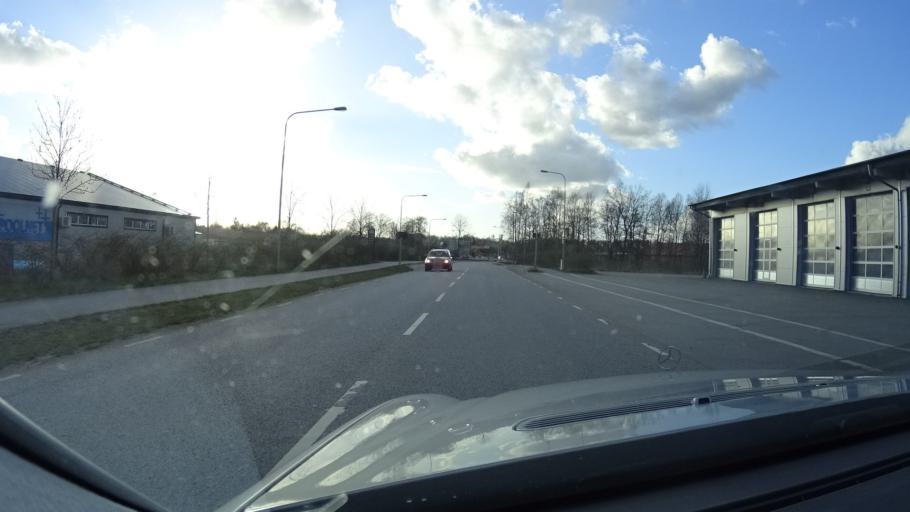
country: SE
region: Skane
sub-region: Hoors Kommun
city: Satofta
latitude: 55.9250
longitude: 13.5491
